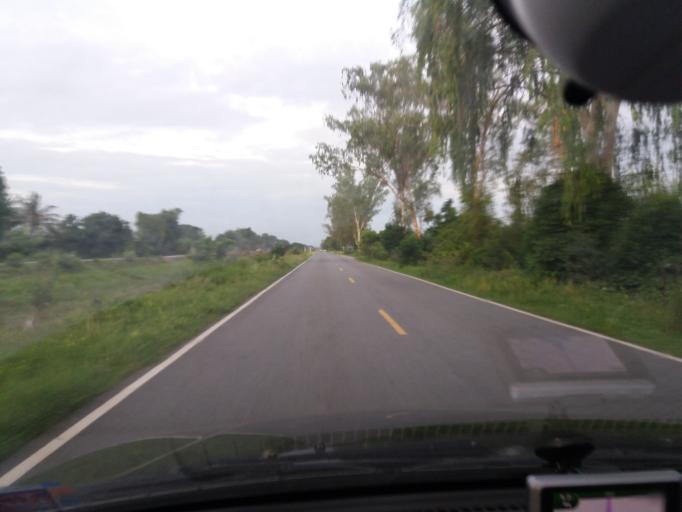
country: TH
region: Suphan Buri
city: Don Chedi
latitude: 14.5499
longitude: 99.9430
